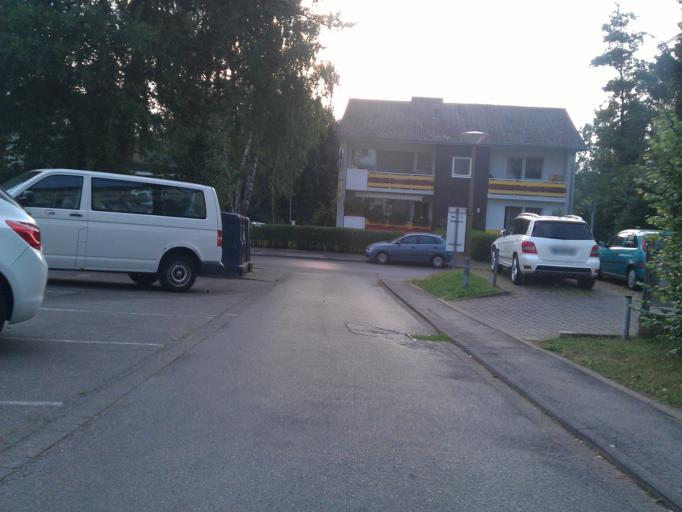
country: DE
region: North Rhine-Westphalia
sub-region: Regierungsbezirk Koln
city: Aachen
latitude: 50.7668
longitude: 6.0706
